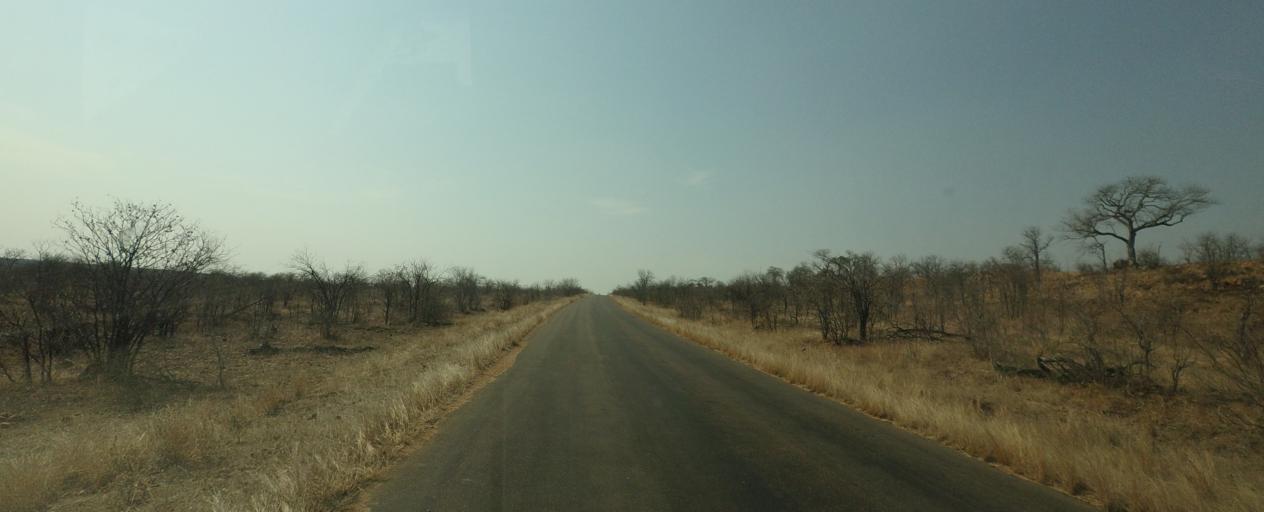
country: ZA
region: Limpopo
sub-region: Mopani District Municipality
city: Phalaborwa
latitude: -23.9630
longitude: 31.6259
